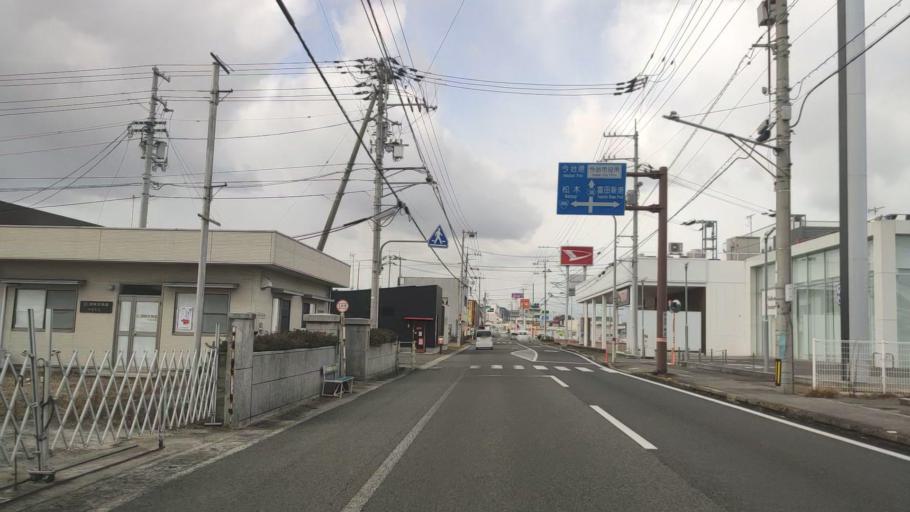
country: JP
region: Ehime
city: Saijo
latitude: 34.0458
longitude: 133.0204
